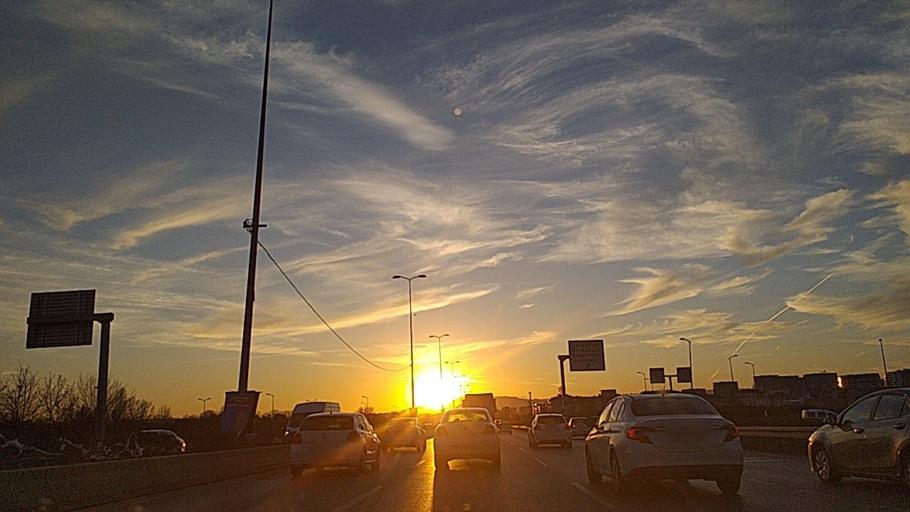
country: TR
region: Ankara
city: Etimesgut
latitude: 39.9631
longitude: 32.6703
